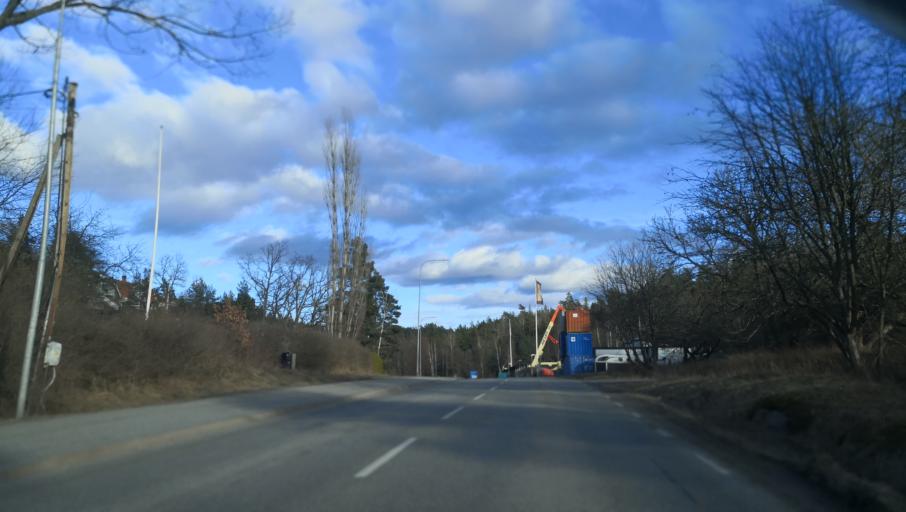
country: SE
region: Stockholm
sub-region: Varmdo Kommun
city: Gustavsberg
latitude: 59.3316
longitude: 18.3413
